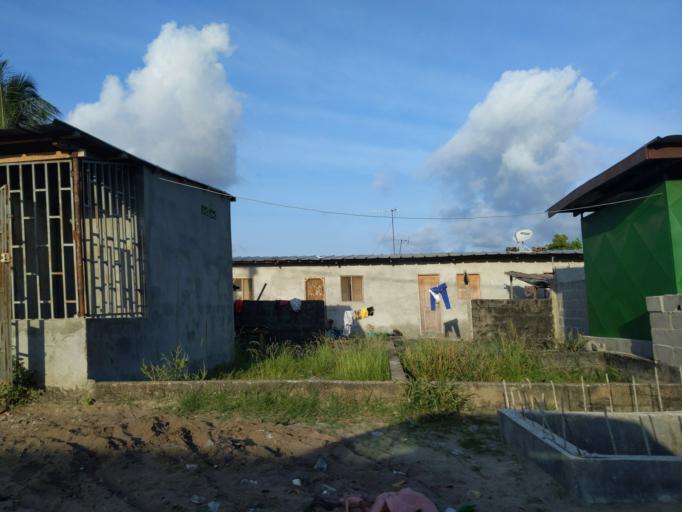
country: CI
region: Sud-Comoe
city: Grand-Bassam
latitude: 5.2210
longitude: -3.7289
